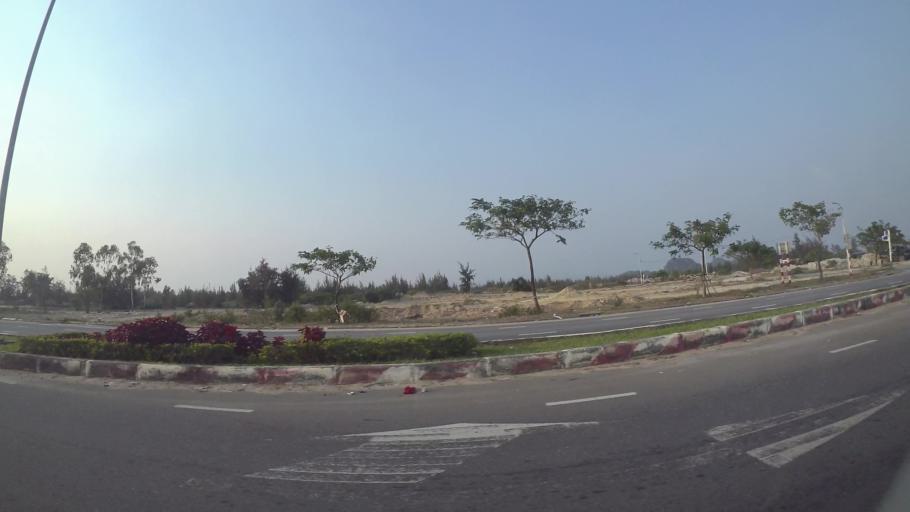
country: VN
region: Da Nang
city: Ngu Hanh Son
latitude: 15.9831
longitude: 108.2457
